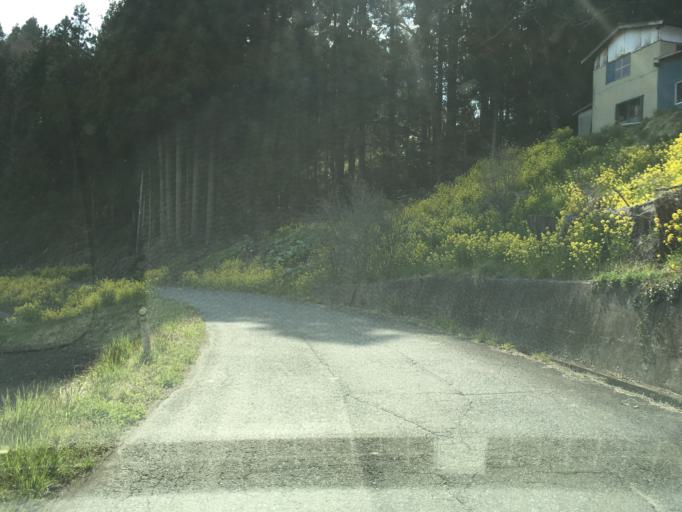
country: JP
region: Iwate
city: Ichinoseki
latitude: 38.8469
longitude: 141.3548
